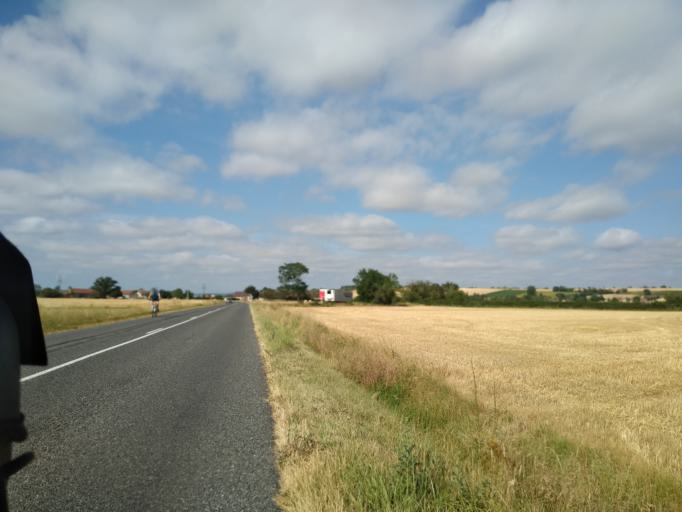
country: FR
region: Auvergne
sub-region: Departement de l'Allier
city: Saint-Pourcain-sur-Sioule
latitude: 46.2836
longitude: 3.2390
